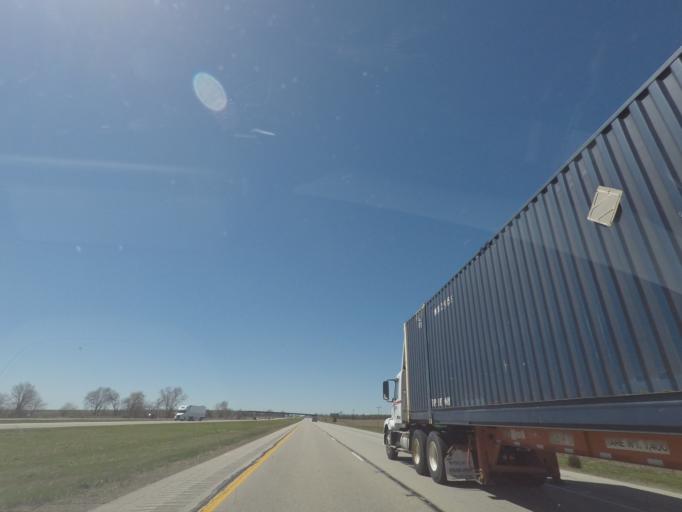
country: US
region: Illinois
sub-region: McLean County
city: Lexington
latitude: 40.6089
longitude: -88.8338
